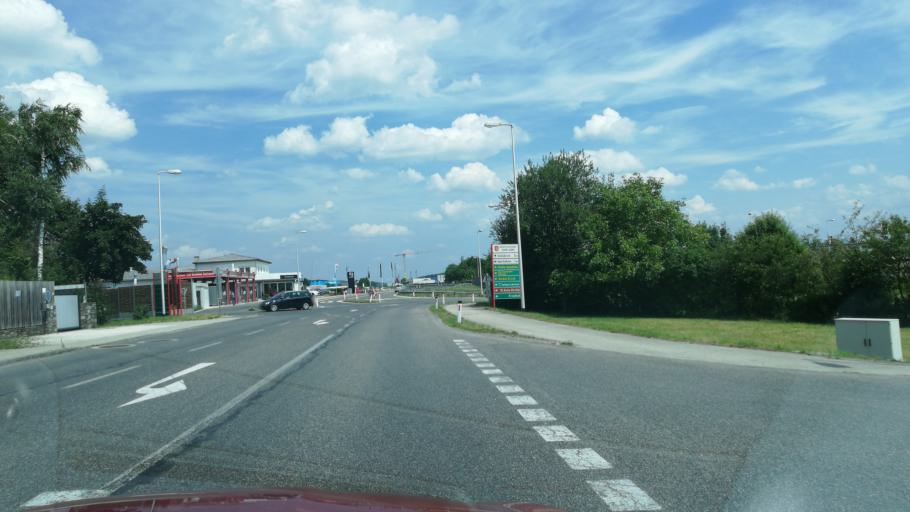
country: AT
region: Upper Austria
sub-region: Politischer Bezirk Vocklabruck
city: Timelkam
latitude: 48.0029
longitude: 13.6275
